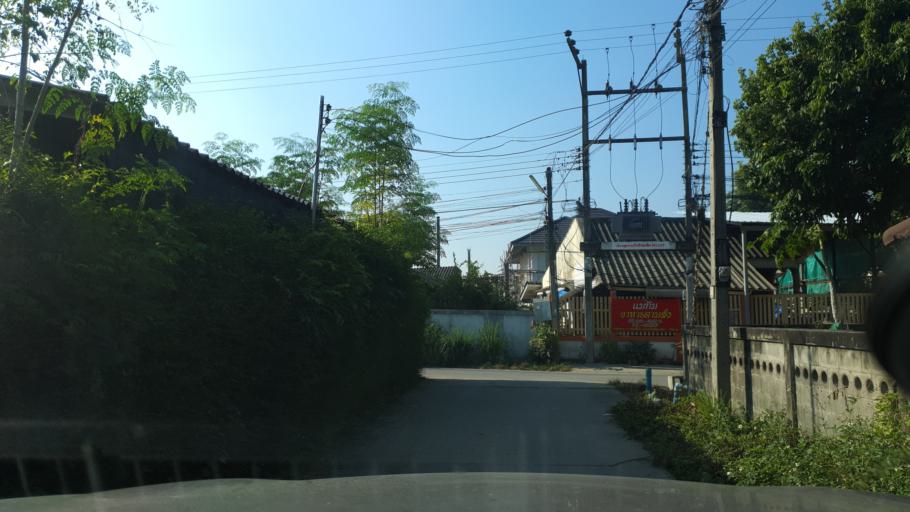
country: TH
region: Chiang Mai
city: San Kamphaeng
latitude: 18.7001
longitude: 99.1608
